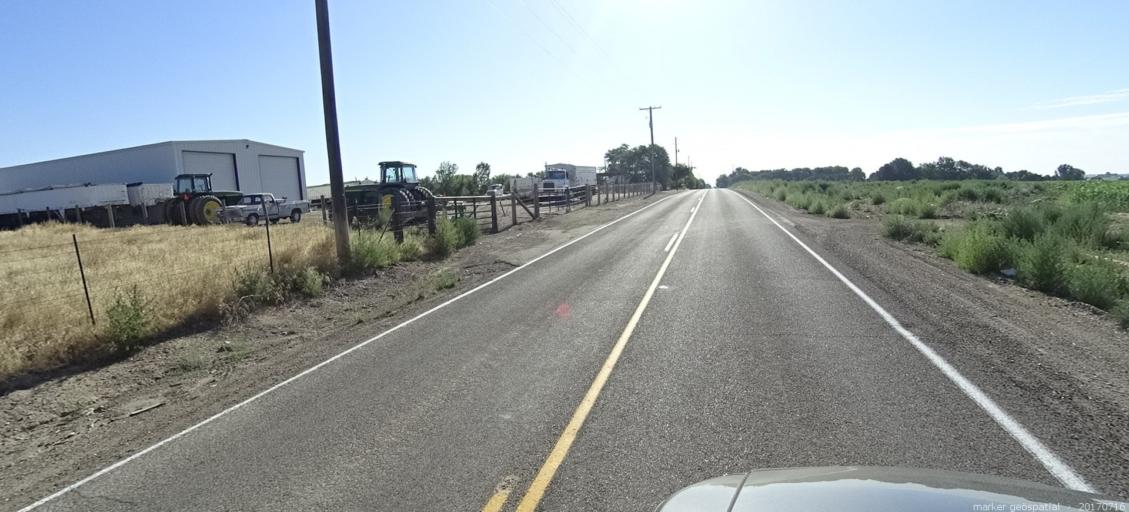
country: US
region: Idaho
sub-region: Ada County
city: Kuna
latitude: 43.5465
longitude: -116.4093
